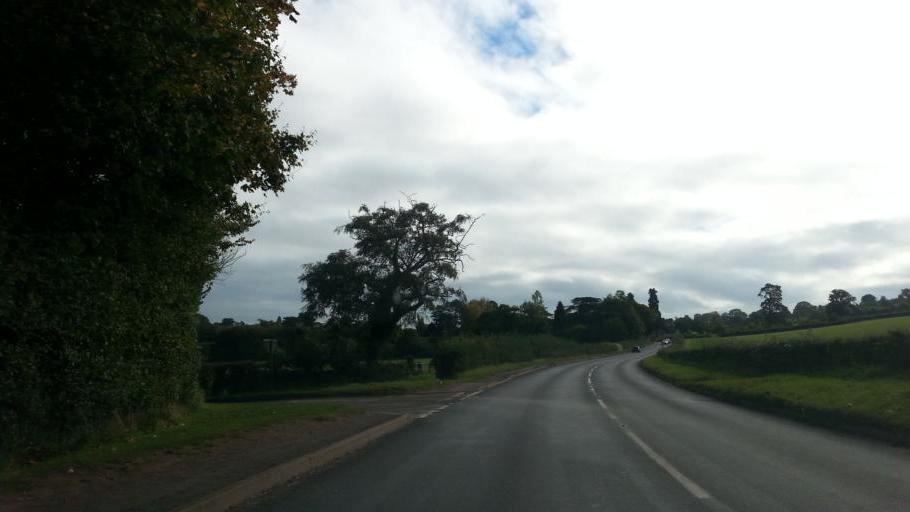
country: GB
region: England
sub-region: Herefordshire
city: Ross on Wye
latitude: 51.9117
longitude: -2.5491
